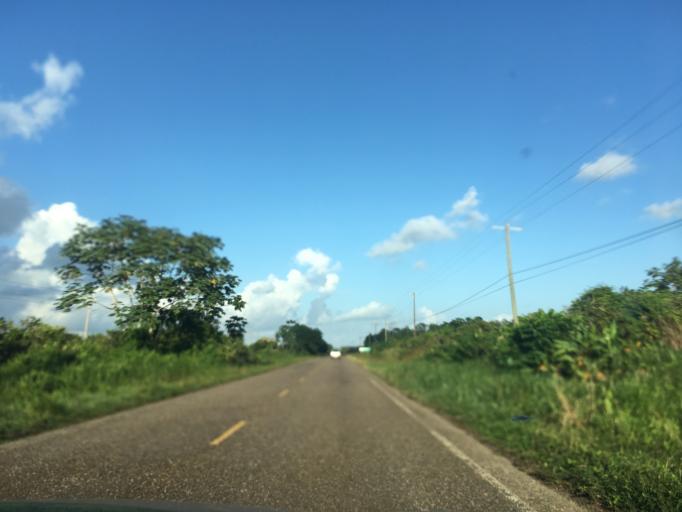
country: BZ
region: Stann Creek
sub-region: Dangriga
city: Dangriga
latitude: 16.8284
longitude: -88.3672
